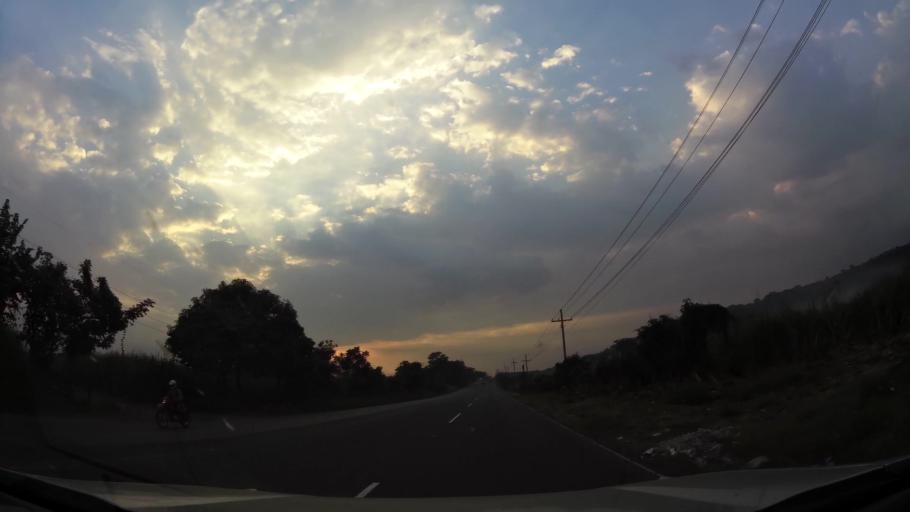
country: GT
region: Escuintla
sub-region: Municipio de Masagua
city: Masagua
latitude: 14.2678
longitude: -90.8743
